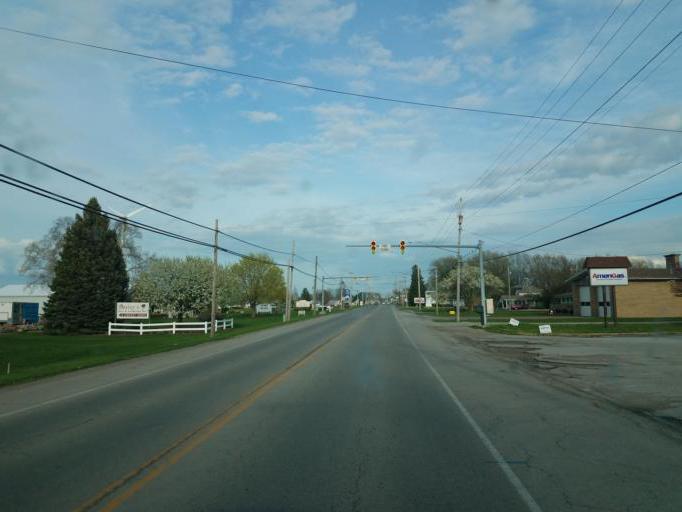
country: US
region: Ohio
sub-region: Erie County
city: Sandusky
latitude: 41.4420
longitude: -82.7558
